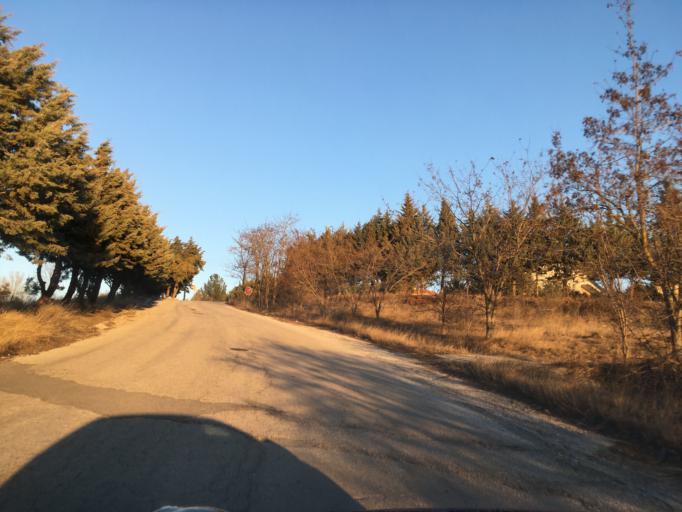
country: GR
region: West Macedonia
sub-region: Nomos Kozanis
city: Koila
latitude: 40.3229
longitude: 21.8188
